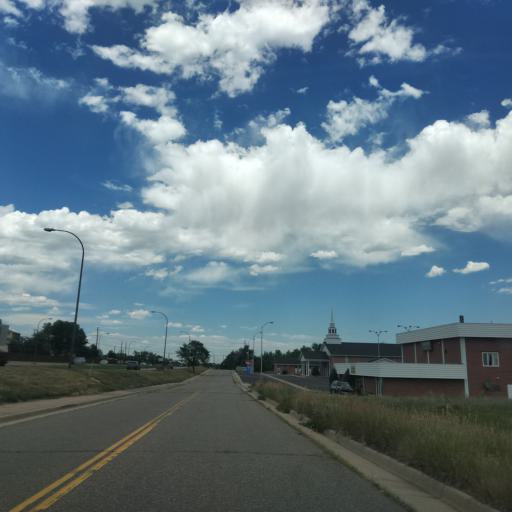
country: US
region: Colorado
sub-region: Jefferson County
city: Lakewood
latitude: 39.7069
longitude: -105.1093
